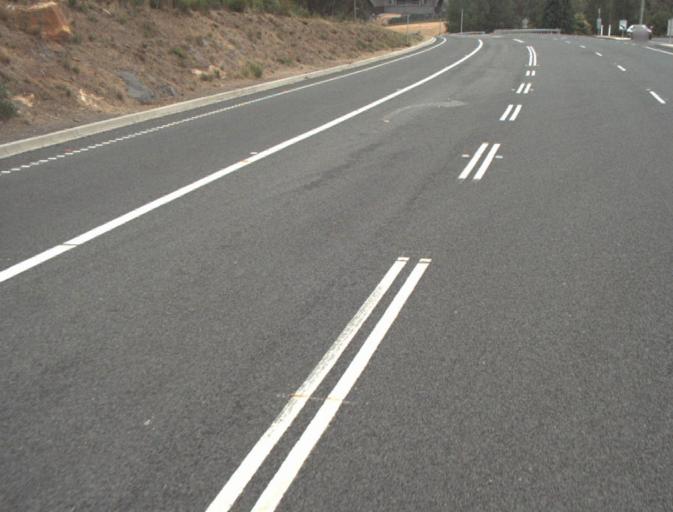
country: AU
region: Tasmania
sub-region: Launceston
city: Mayfield
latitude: -41.2665
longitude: 147.0333
